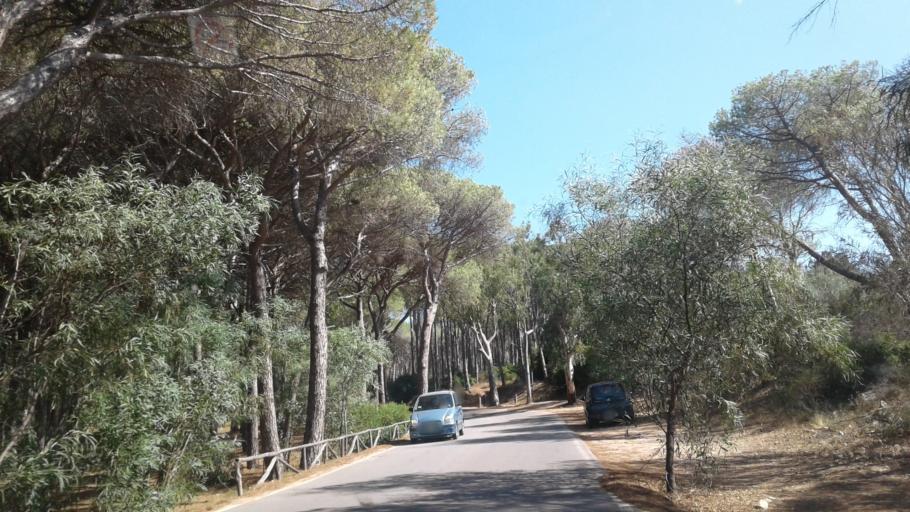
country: IT
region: Sardinia
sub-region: Provincia di Olbia-Tempio
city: La Maddalena
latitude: 41.2112
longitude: 9.4556
